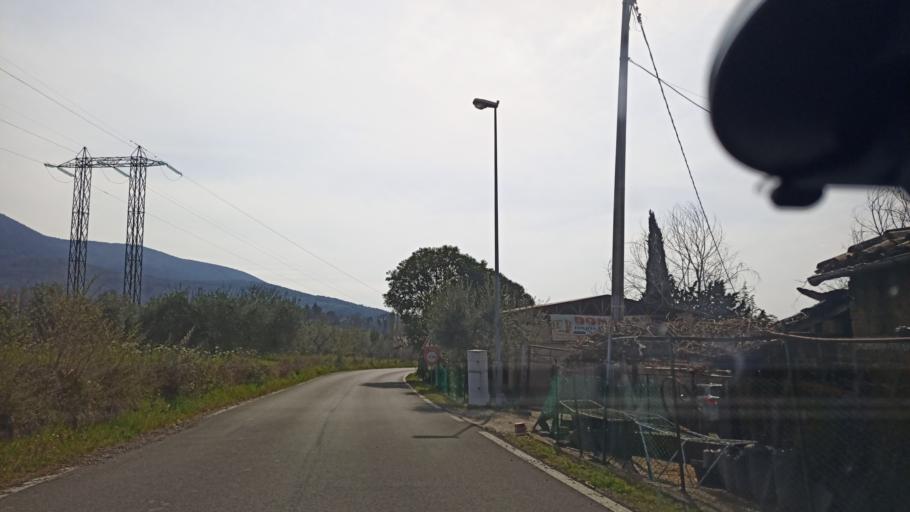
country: IT
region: Latium
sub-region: Provincia di Rieti
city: Montasola
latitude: 42.3668
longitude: 12.6763
